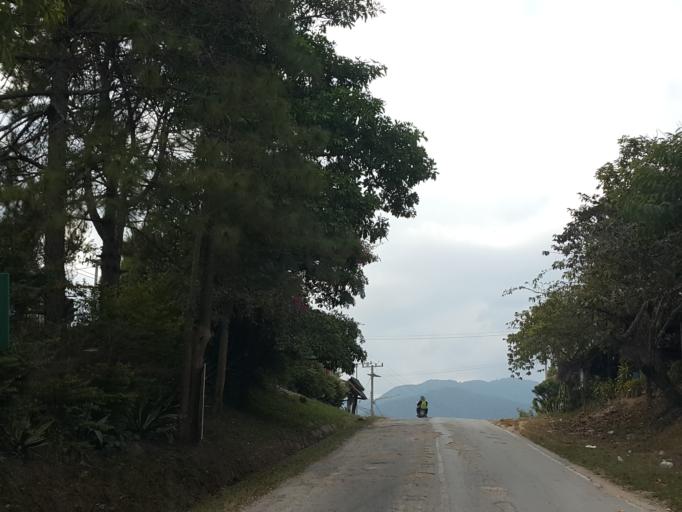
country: TH
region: Chiang Mai
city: Om Koi
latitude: 17.7999
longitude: 98.3391
